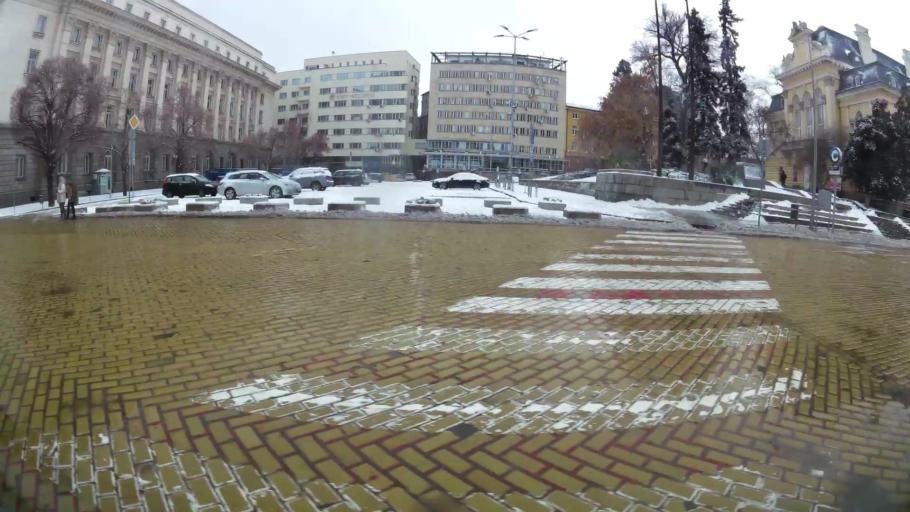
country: BG
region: Sofia-Capital
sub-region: Stolichna Obshtina
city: Sofia
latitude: 42.6964
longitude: 23.3260
